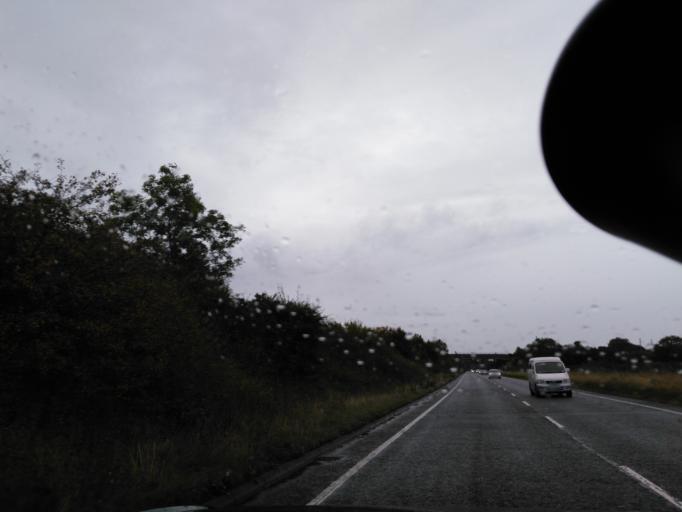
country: GB
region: England
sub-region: Wiltshire
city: Chippenham
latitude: 51.4414
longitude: -2.1426
